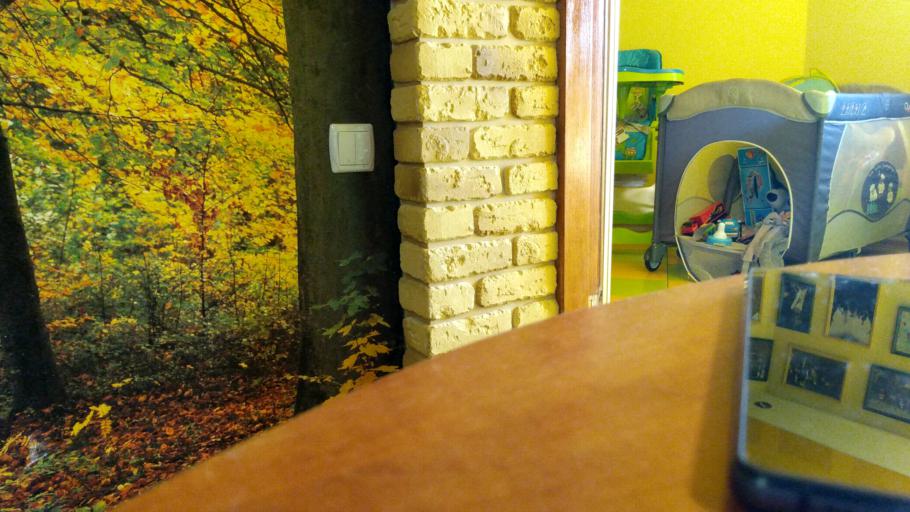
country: RU
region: Tverskaya
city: Kalashnikovo
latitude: 57.2940
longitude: 35.3491
